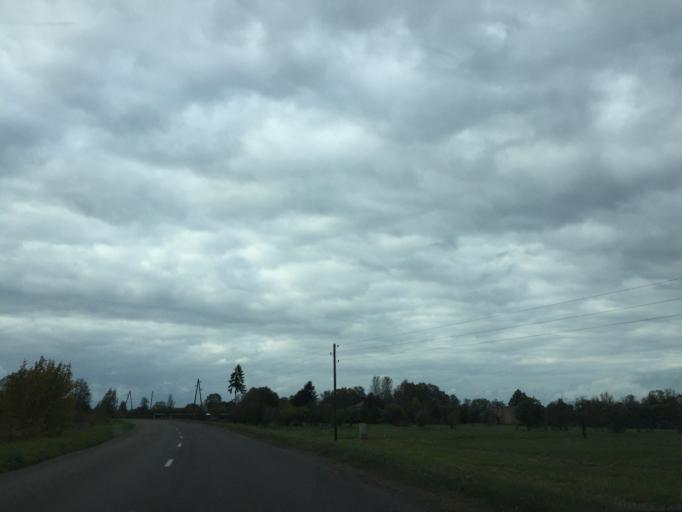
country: LV
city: Tireli
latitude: 56.8019
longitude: 23.5985
